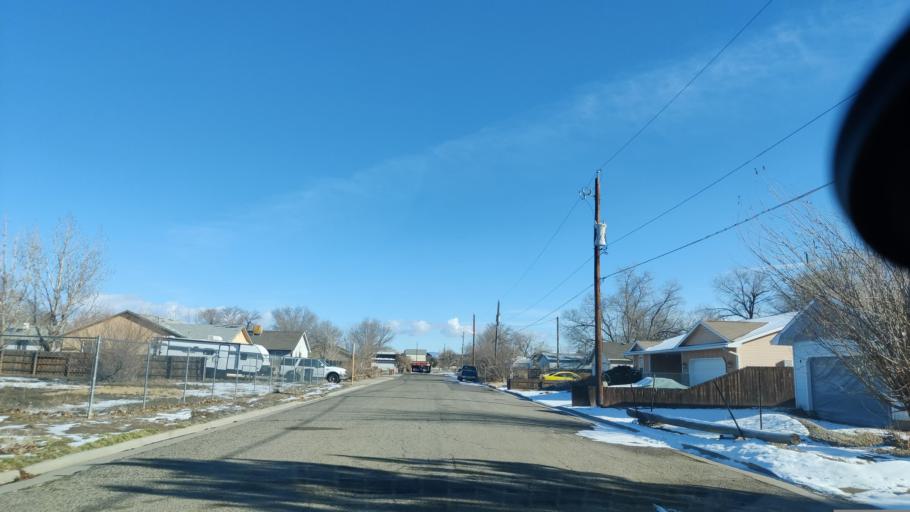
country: US
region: Colorado
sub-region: Mesa County
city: Fruita
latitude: 39.1571
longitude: -108.7236
